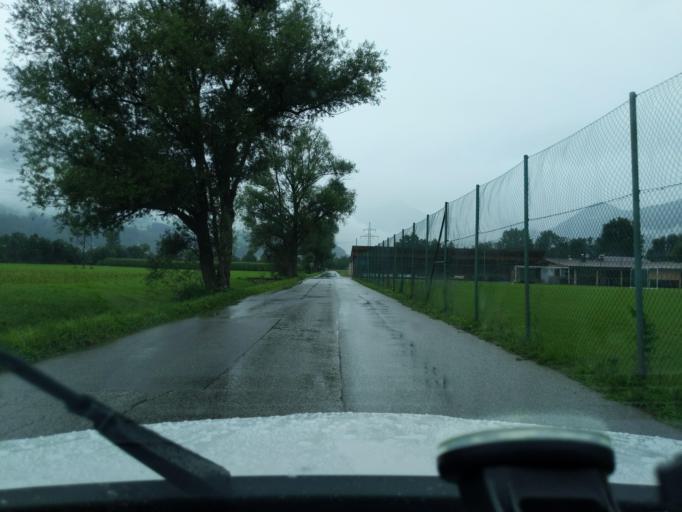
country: AT
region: Tyrol
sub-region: Politischer Bezirk Schwaz
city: Hart im Zillertal
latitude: 47.3417
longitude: 11.8653
